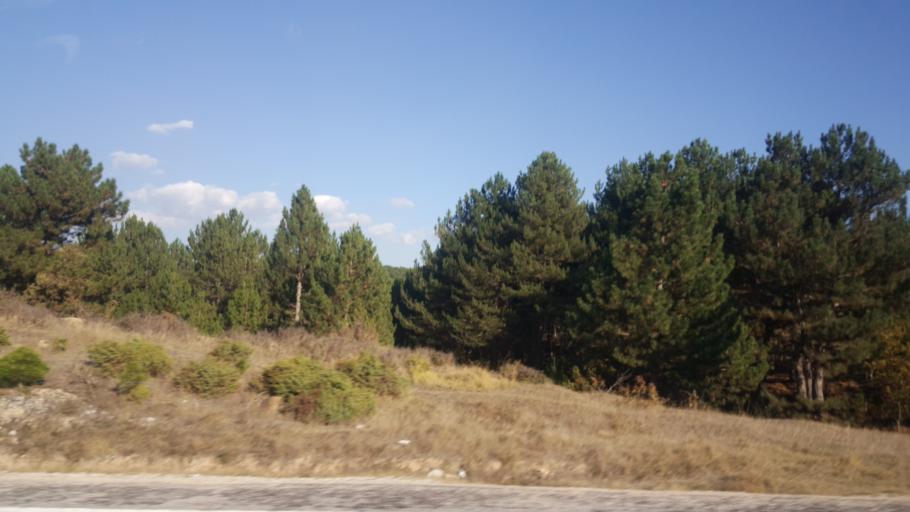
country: TR
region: Eskisehir
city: Kirka
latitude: 39.1160
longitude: 30.5881
